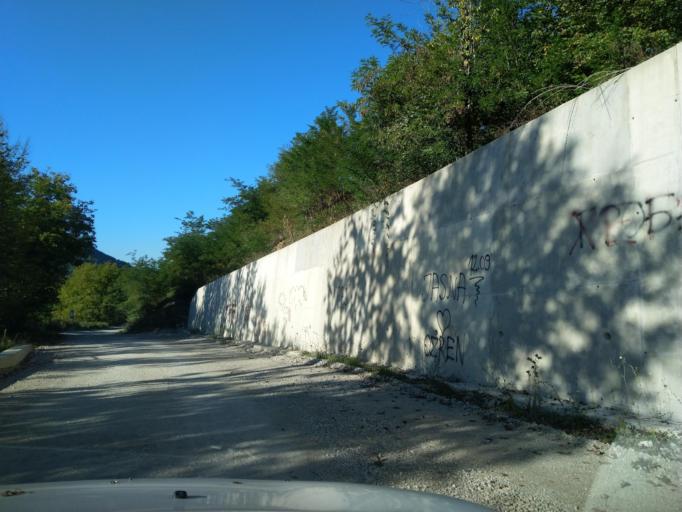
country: RS
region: Central Serbia
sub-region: Moravicki Okrug
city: Ivanjica
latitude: 43.4754
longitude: 20.2387
